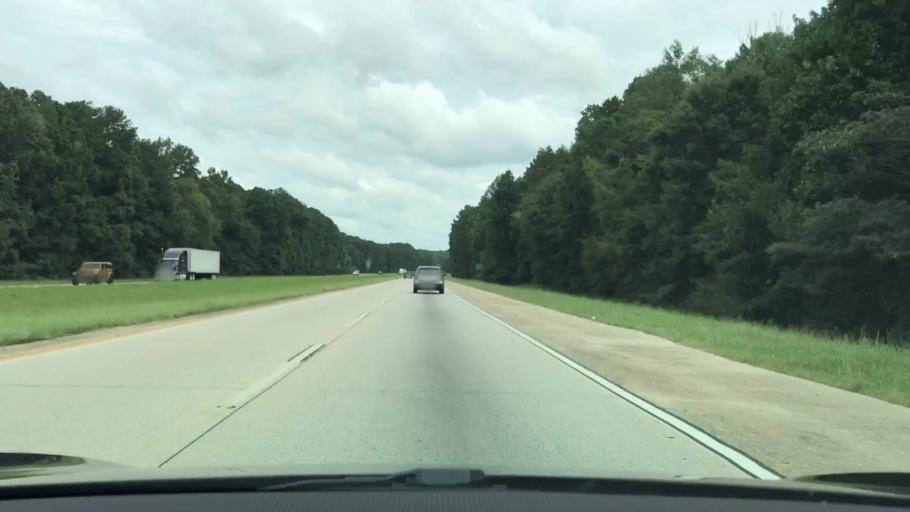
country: US
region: Georgia
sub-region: Troup County
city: La Grange
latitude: 33.0082
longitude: -85.0009
